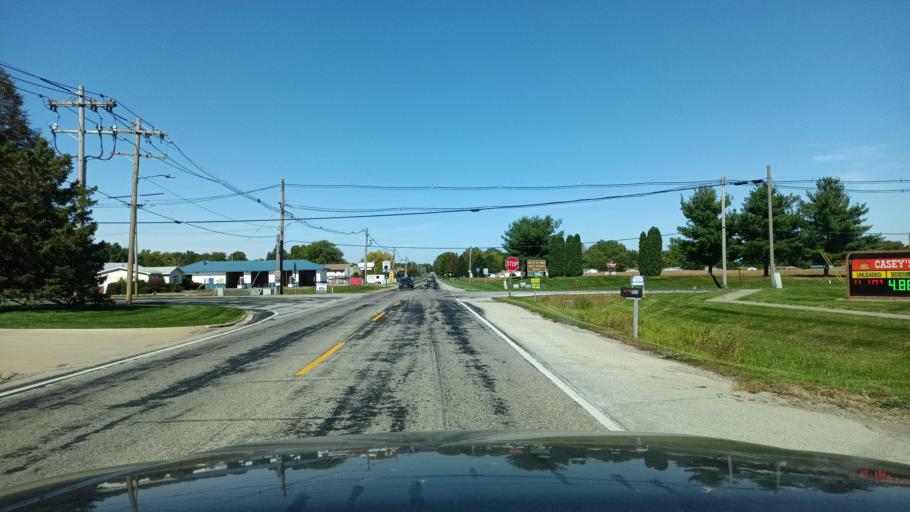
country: US
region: Illinois
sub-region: Champaign County
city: Lake of the Woods
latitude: 40.1960
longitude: -88.3653
